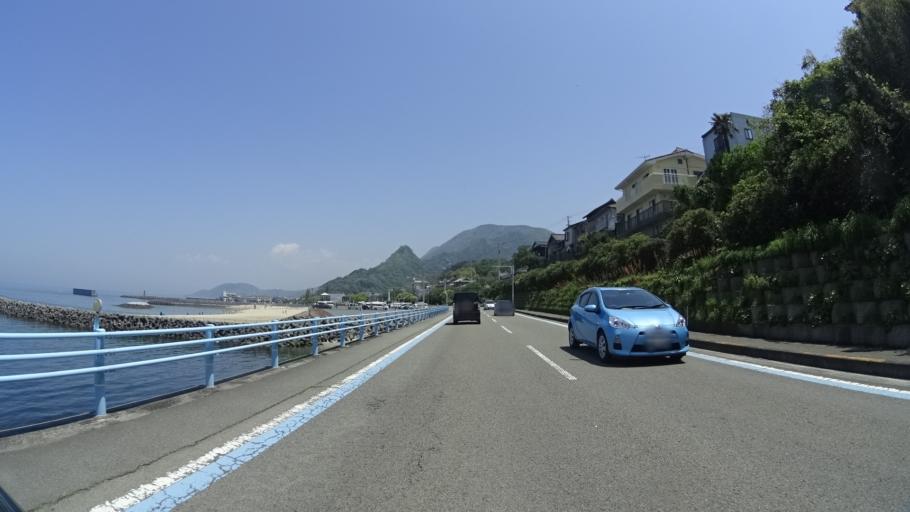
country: JP
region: Ehime
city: Iyo
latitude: 33.6842
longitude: 132.6320
